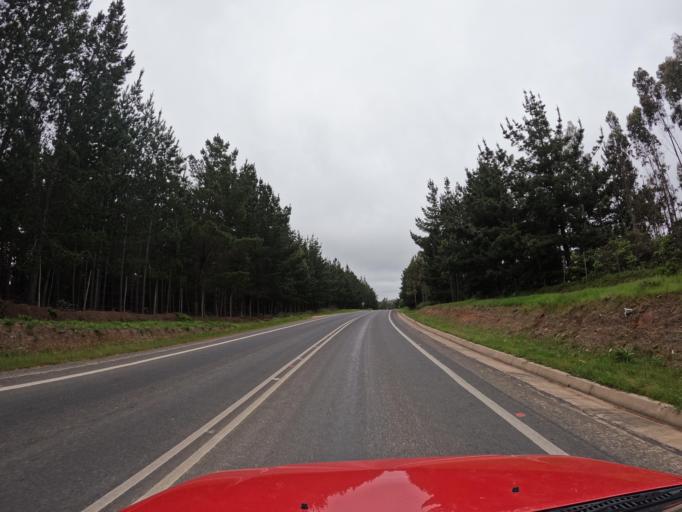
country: CL
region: O'Higgins
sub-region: Provincia de Colchagua
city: Santa Cruz
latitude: -34.5999
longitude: -72.0166
